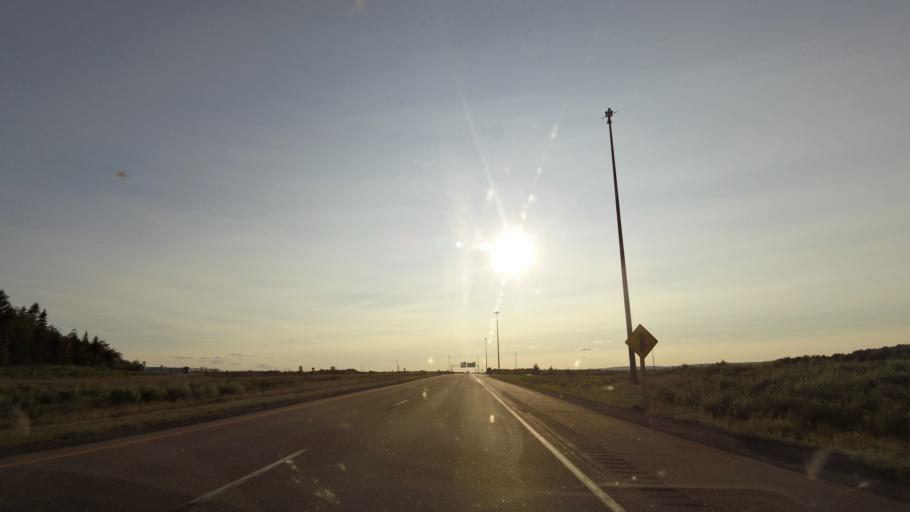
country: CA
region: New Brunswick
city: Dieppe
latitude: 46.1291
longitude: -64.6739
